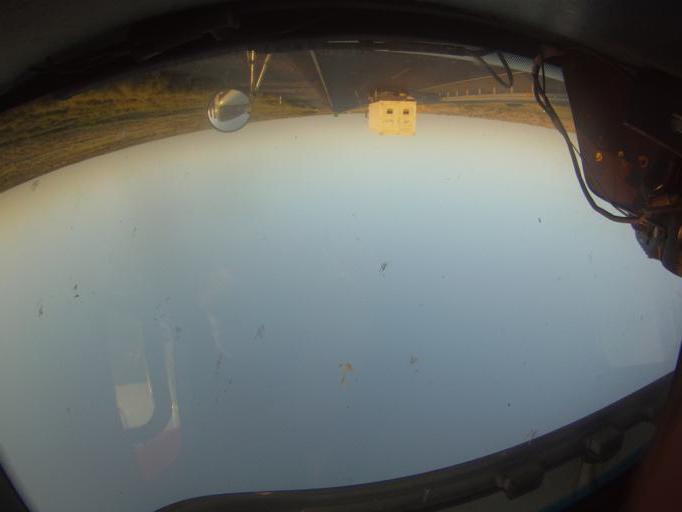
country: KZ
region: Qyzylorda
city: Zhangaqorghan
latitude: 44.0740
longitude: 67.1361
